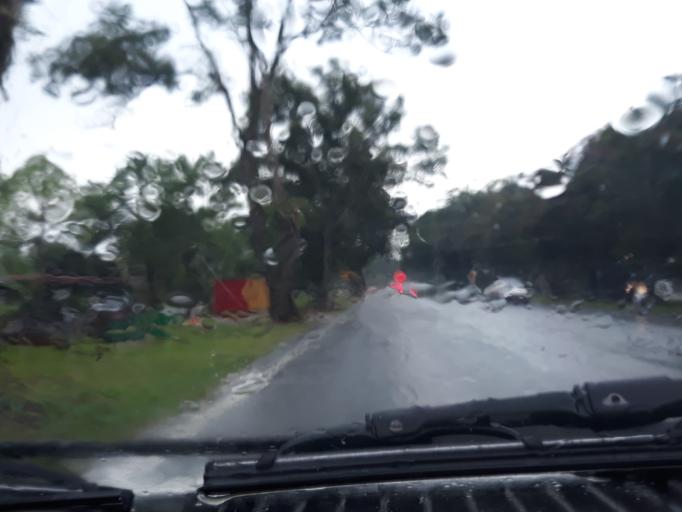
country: MY
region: Kedah
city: Kulim
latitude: 5.3709
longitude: 100.5813
